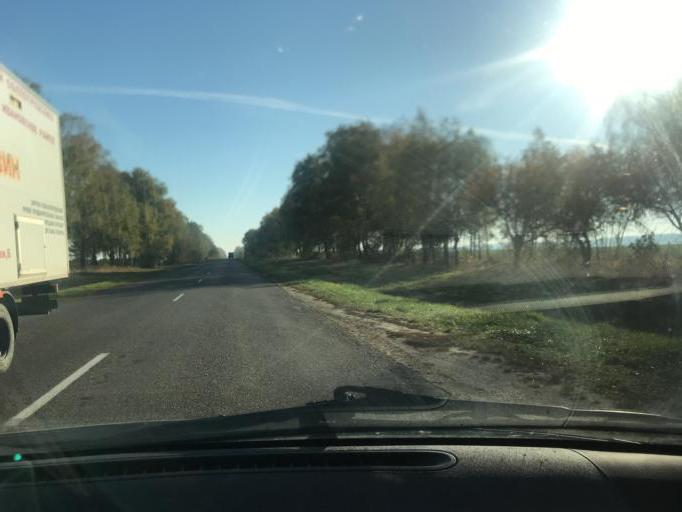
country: BY
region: Brest
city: Ivanava
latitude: 52.1453
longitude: 25.4776
